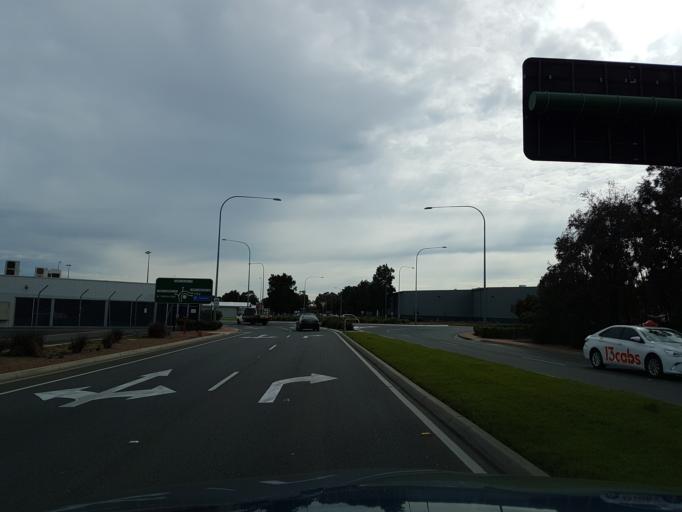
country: AU
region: South Australia
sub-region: City of West Torrens
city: Plympton
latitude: -34.9362
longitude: 138.5347
